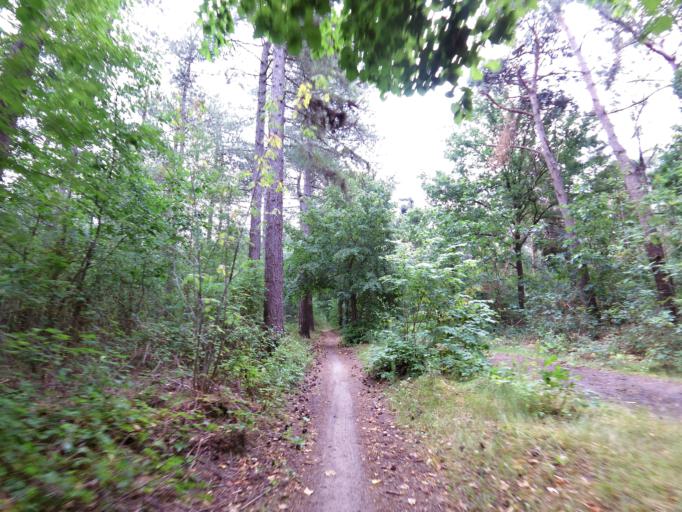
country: NL
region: North Brabant
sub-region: Gemeente Breda
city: Hoge Vucht
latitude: 51.6385
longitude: 4.8136
